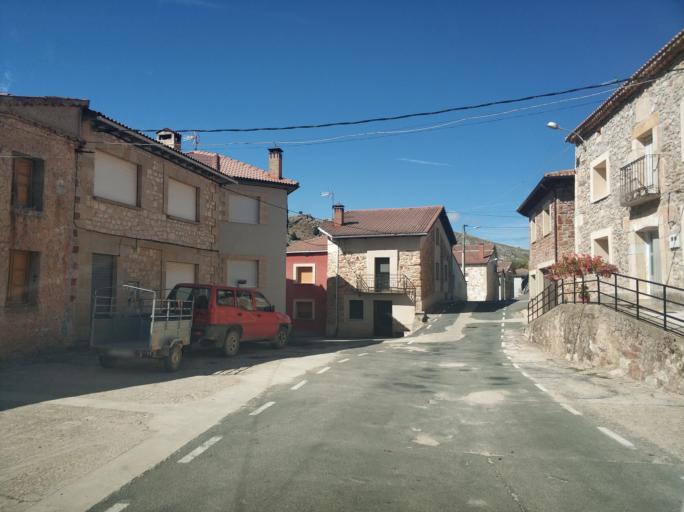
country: ES
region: Castille and Leon
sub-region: Provincia de Soria
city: Espeja de San Marcelino
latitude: 41.8024
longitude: -3.2213
